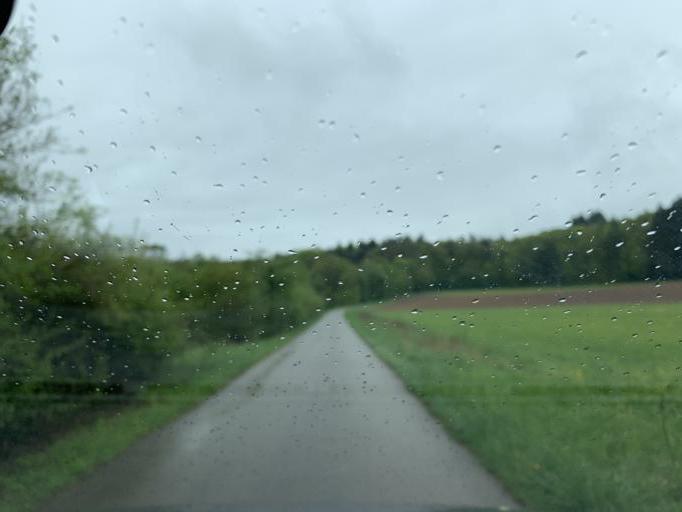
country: CH
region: Schaffhausen
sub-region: Bezirk Schaffhausen
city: Beringen
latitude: 47.7077
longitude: 8.5968
